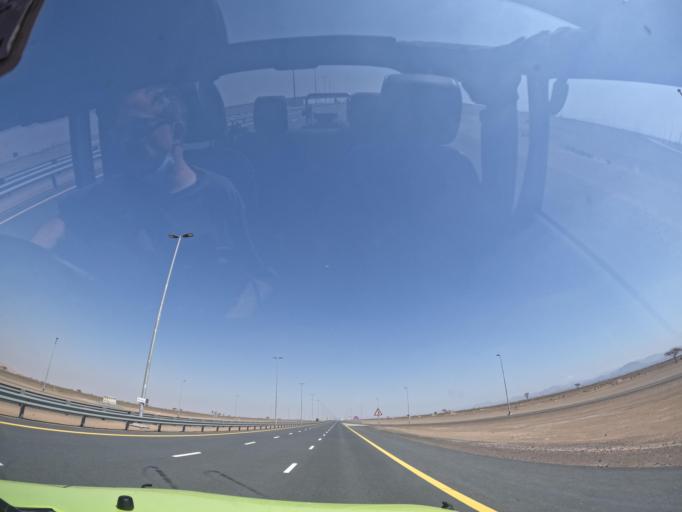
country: AE
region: Ash Shariqah
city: Adh Dhayd
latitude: 25.0497
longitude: 55.8949
